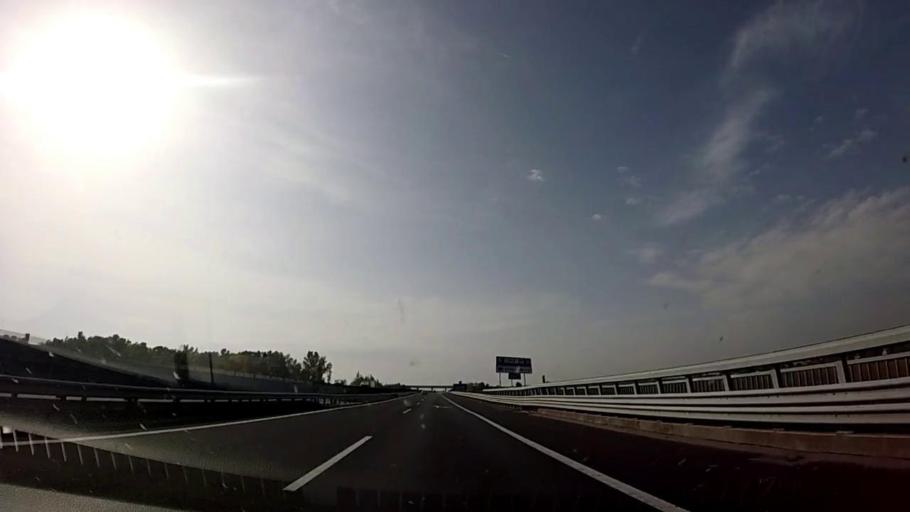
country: HU
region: Zala
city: Murakeresztur
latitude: 46.4622
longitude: 16.8906
